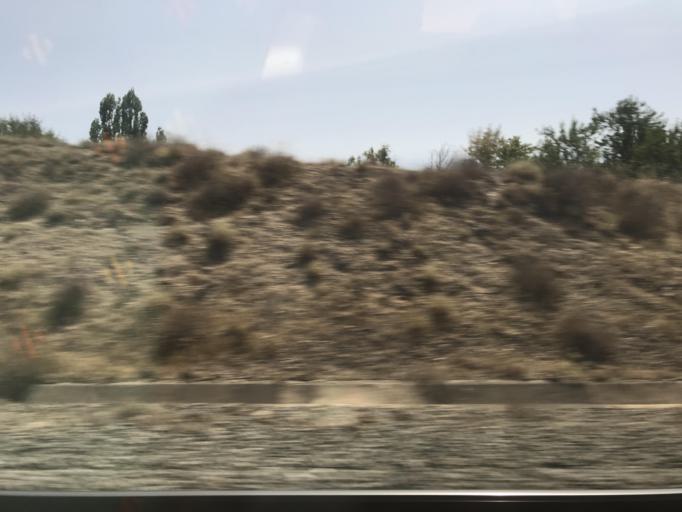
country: ES
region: Castille and Leon
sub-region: Provincia de Palencia
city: Soto de Cerrato
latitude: 41.9511
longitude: -4.4571
